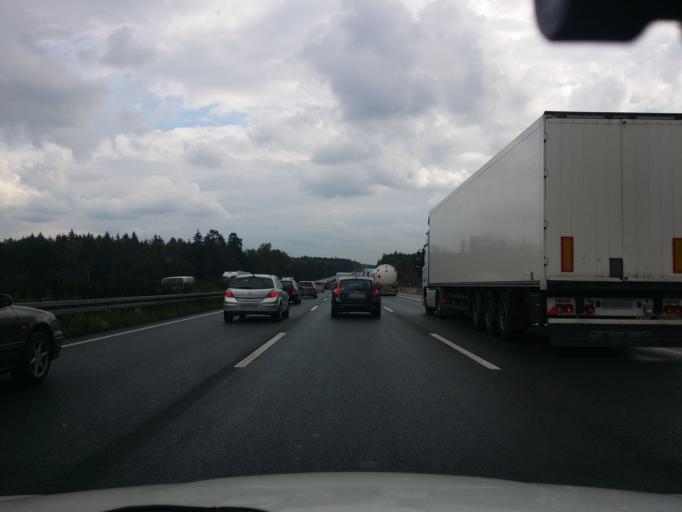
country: DE
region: Thuringia
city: Hainspitz
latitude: 50.9270
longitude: 11.8385
